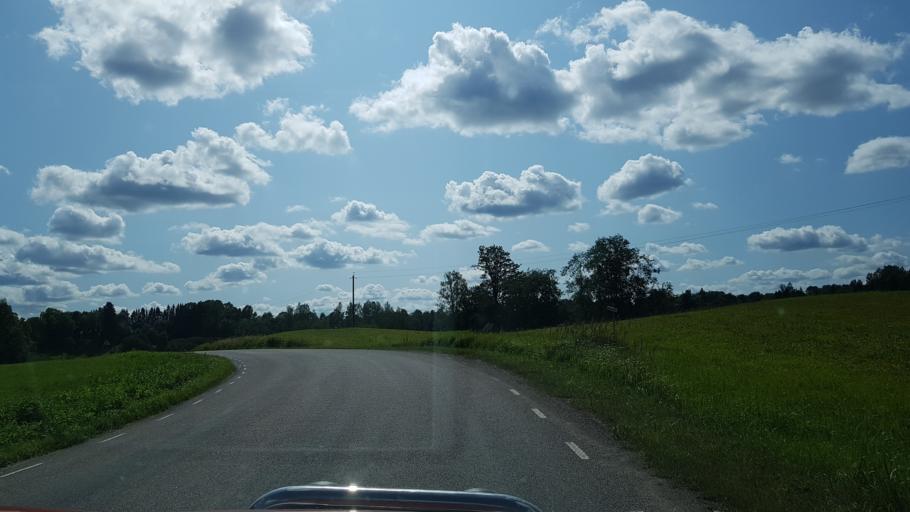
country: EE
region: Vorumaa
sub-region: Voru linn
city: Voru
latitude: 57.6781
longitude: 27.0802
